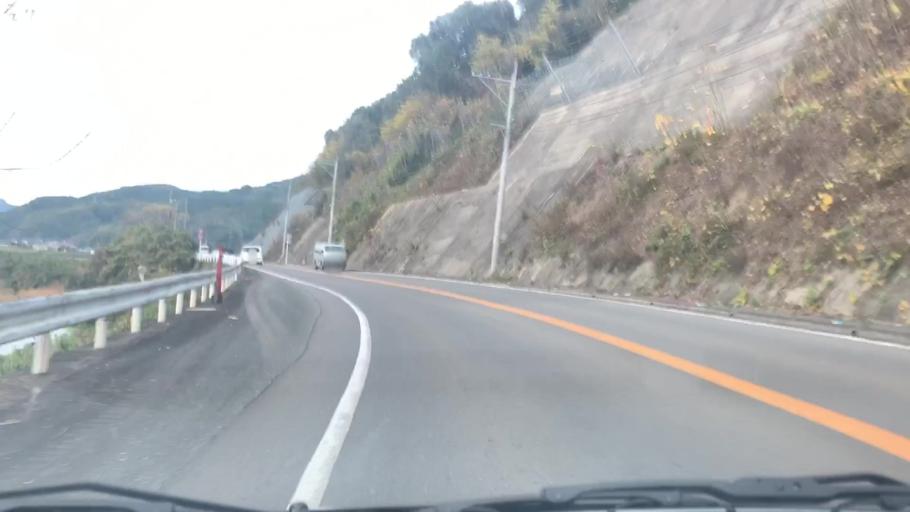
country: JP
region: Saga Prefecture
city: Ureshinomachi-shimojuku
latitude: 33.1369
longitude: 130.0238
